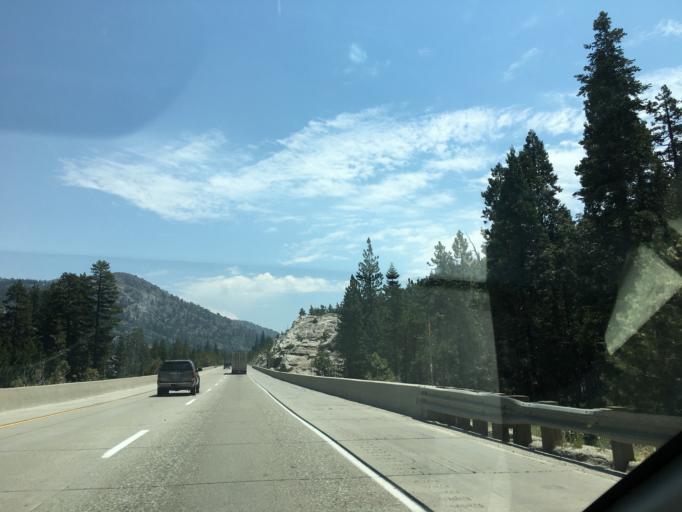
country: US
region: California
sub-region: Sierra County
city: Downieville
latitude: 39.3296
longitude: -120.5839
